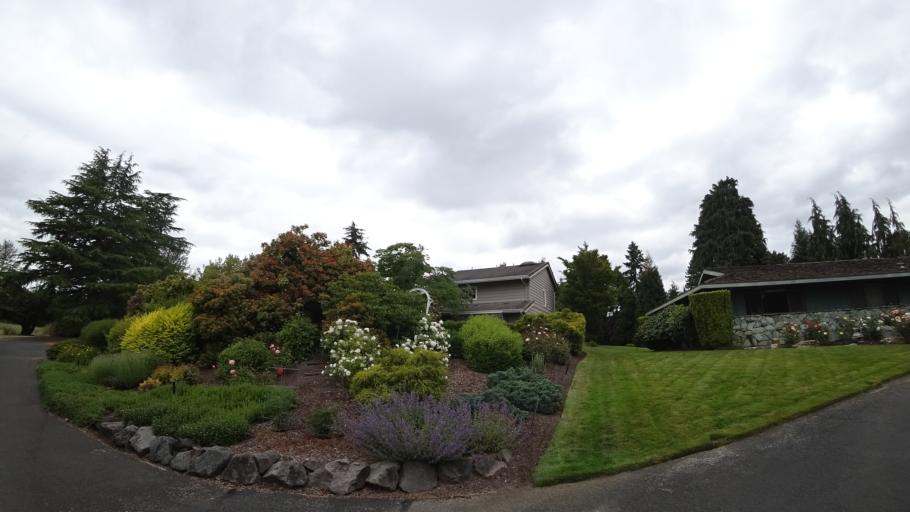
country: US
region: Washington
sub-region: Clark County
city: Vancouver
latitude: 45.5938
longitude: -122.6500
